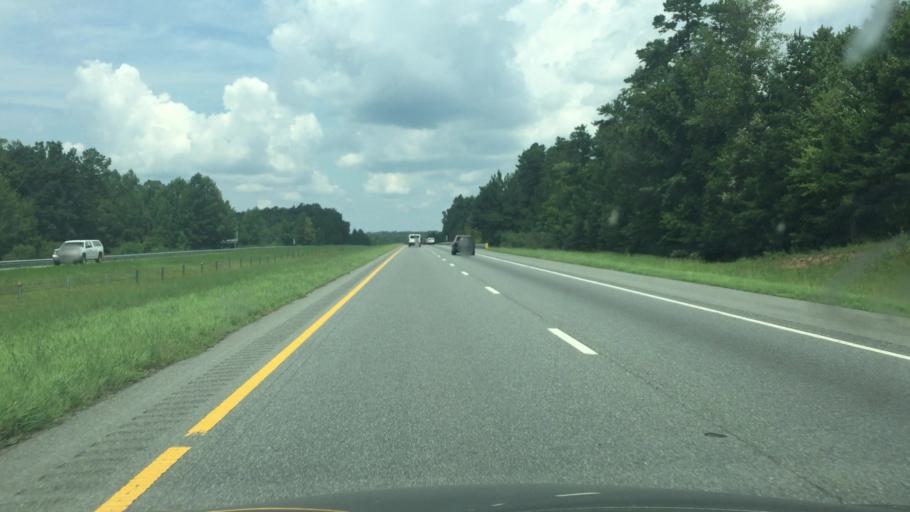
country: US
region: North Carolina
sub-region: Randolph County
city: Asheboro
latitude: 35.5512
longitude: -79.7984
